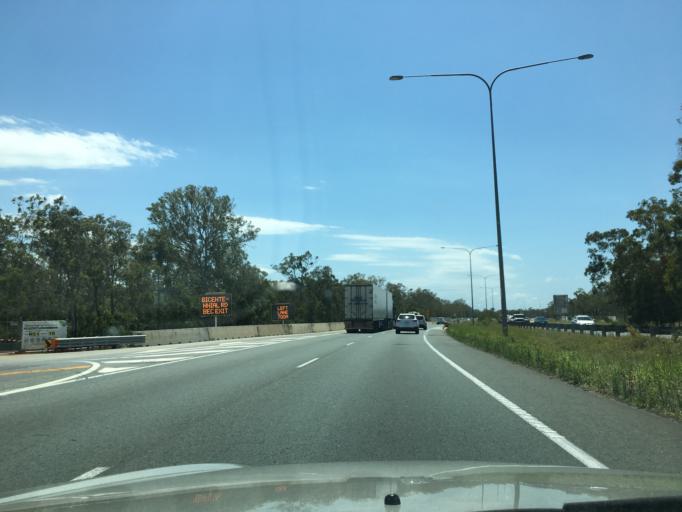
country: AU
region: Queensland
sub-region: Brisbane
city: Deagon
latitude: -27.3525
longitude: 153.0783
